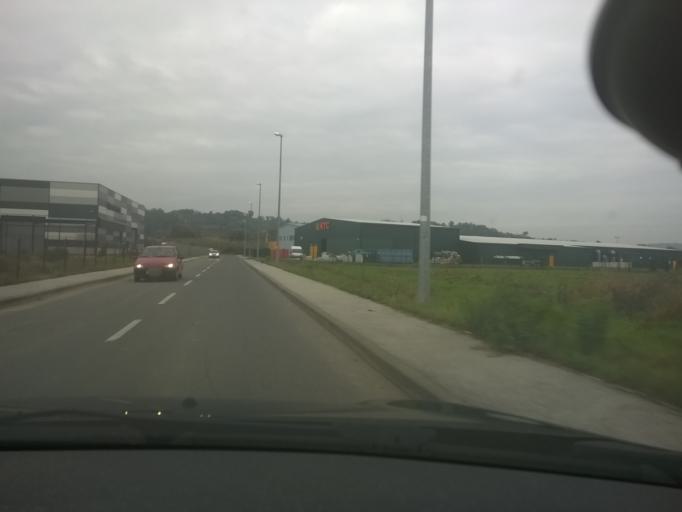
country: HR
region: Krapinsko-Zagorska
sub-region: Grad Krapina
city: Krapina
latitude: 46.1465
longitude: 15.8717
